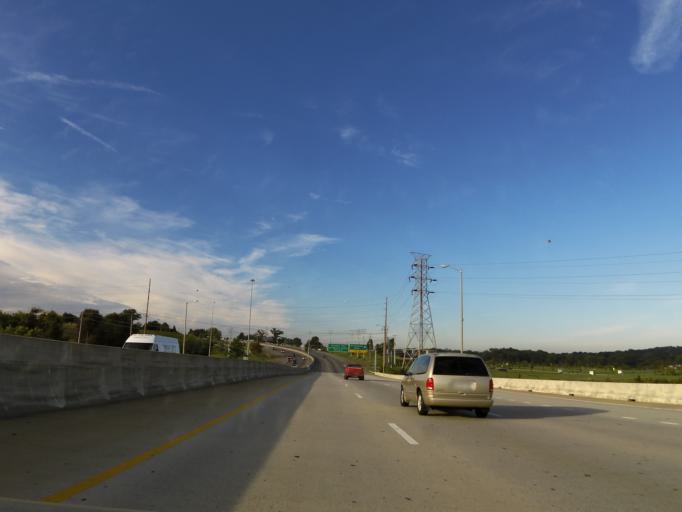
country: US
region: Tennessee
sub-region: Knox County
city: Knoxville
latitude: 35.9470
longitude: -83.9461
